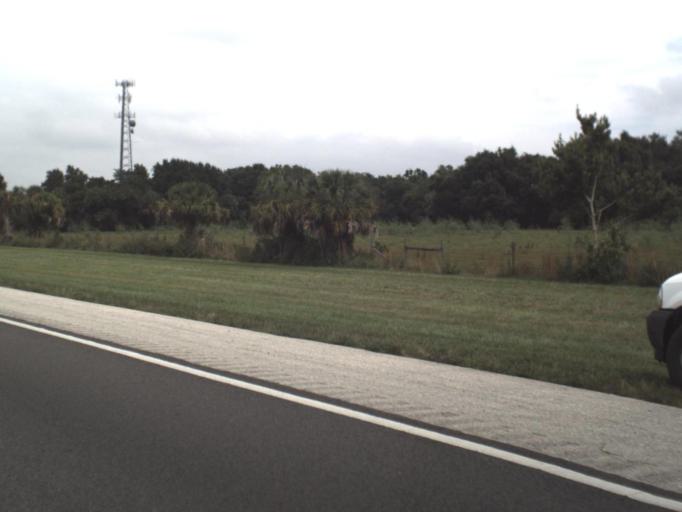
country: US
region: Florida
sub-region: Manatee County
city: Ellenton
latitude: 27.5631
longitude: -82.5126
